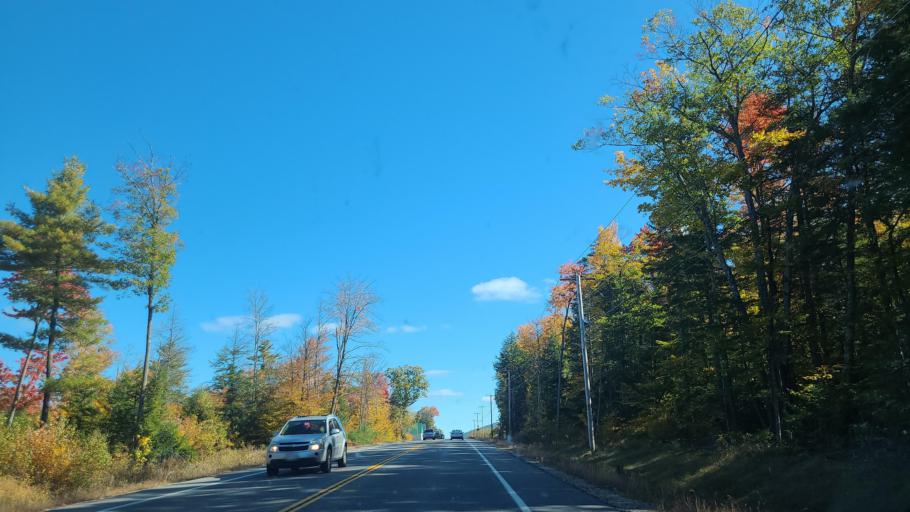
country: US
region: Maine
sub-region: Oxford County
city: Fryeburg
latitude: 44.0268
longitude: -70.9301
